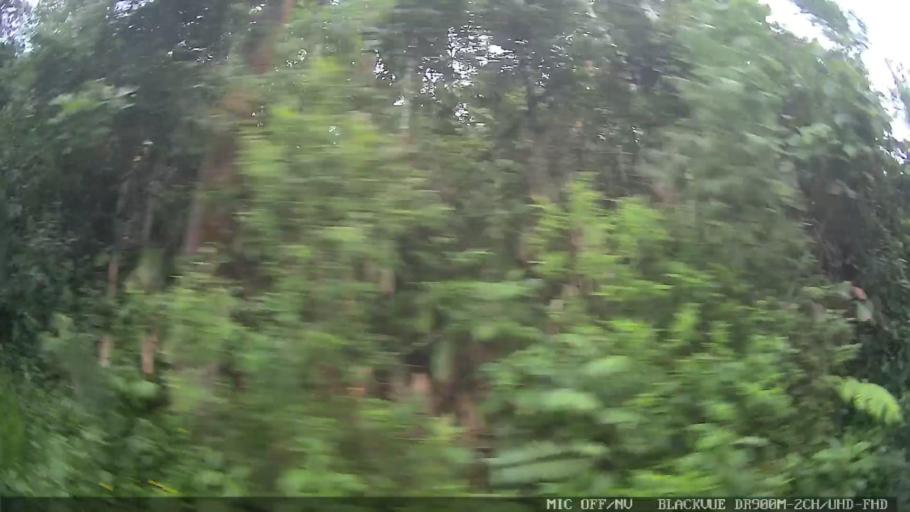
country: BR
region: Sao Paulo
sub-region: Ribeirao Pires
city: Ribeirao Pires
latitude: -23.6944
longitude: -46.4138
